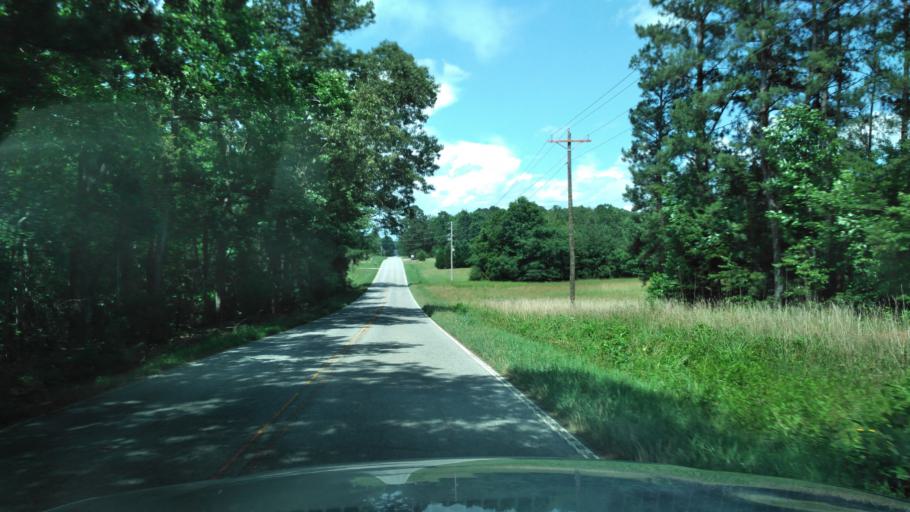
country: US
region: South Carolina
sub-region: Laurens County
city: Laurens
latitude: 34.4846
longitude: -82.1226
